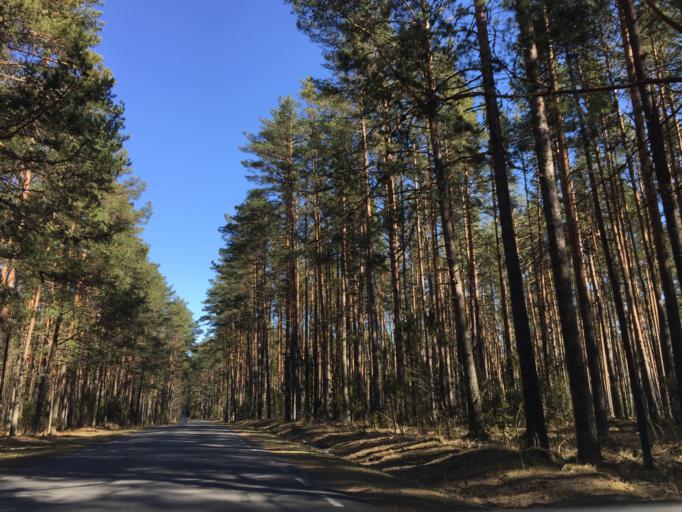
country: EE
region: Tartu
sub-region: Alatskivi vald
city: Kallaste
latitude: 58.9998
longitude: 27.3053
